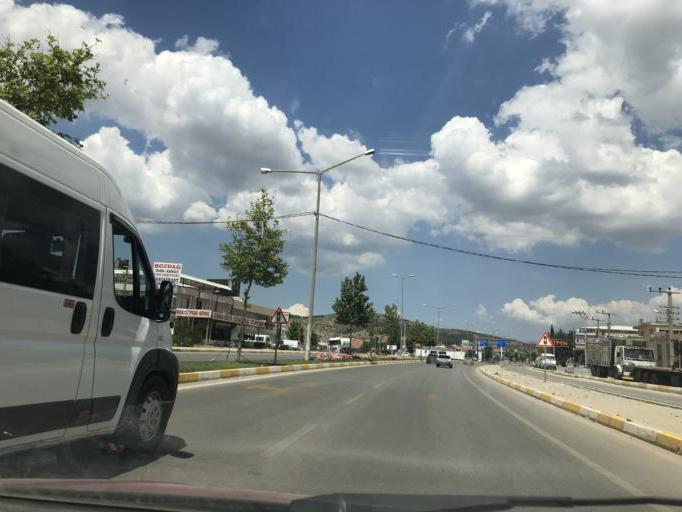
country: TR
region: Denizli
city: Tavas
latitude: 37.5627
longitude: 29.0618
